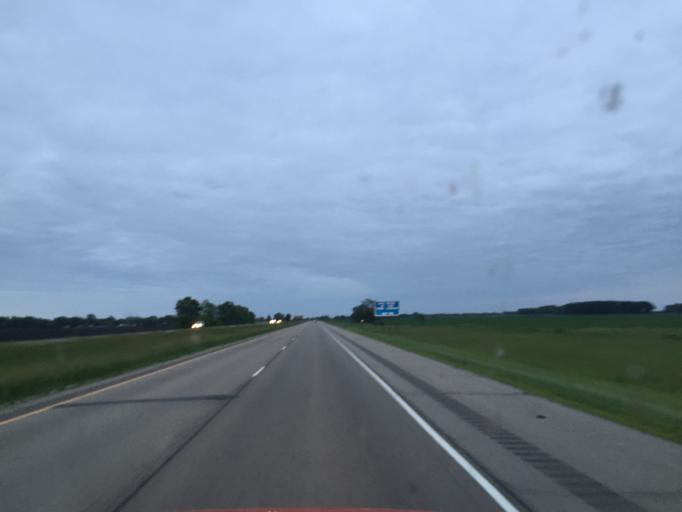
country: US
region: Minnesota
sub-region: Mower County
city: Austin
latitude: 43.6596
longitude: -93.0403
